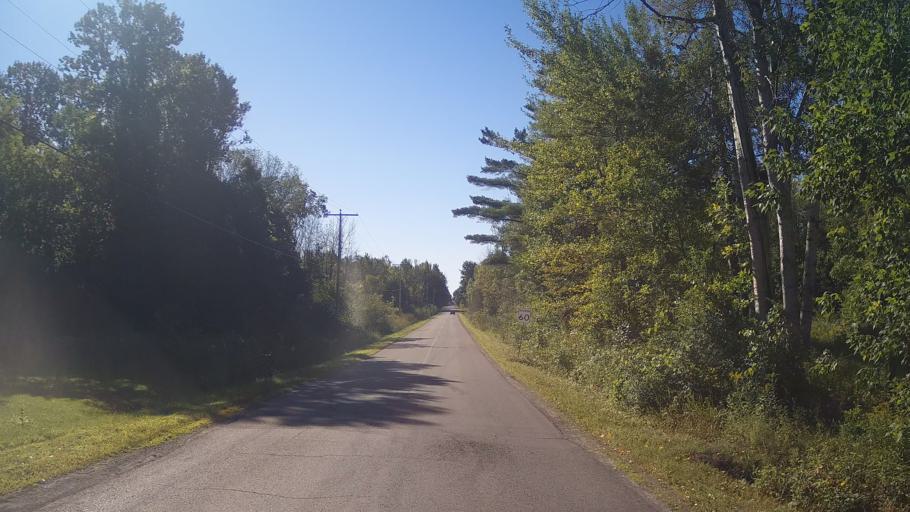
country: CA
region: Ontario
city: Prescott
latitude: 45.0174
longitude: -75.6155
